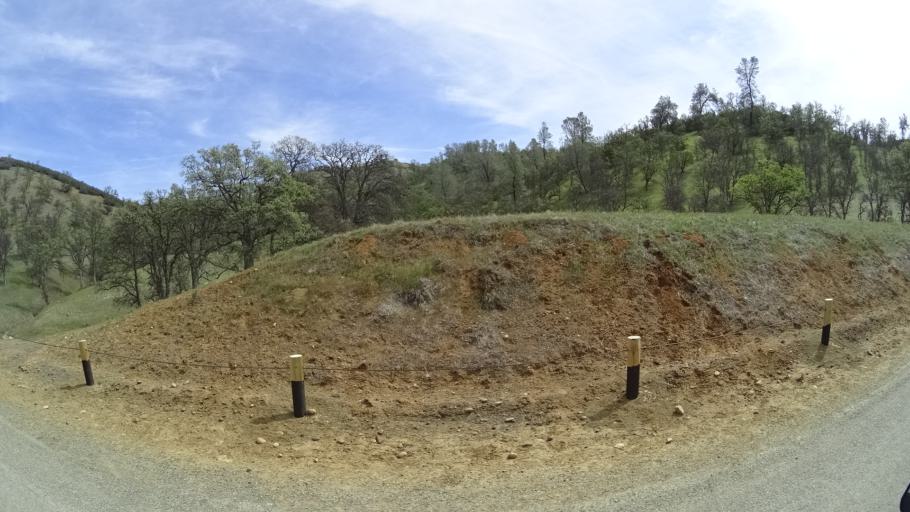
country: US
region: California
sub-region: Glenn County
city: Willows
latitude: 39.5895
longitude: -122.5234
